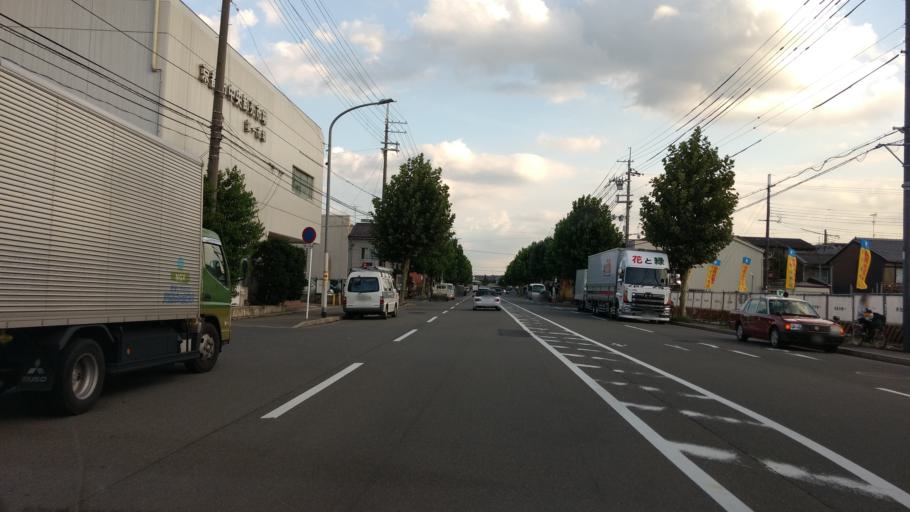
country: JP
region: Kyoto
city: Kyoto
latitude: 34.9921
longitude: 135.7392
